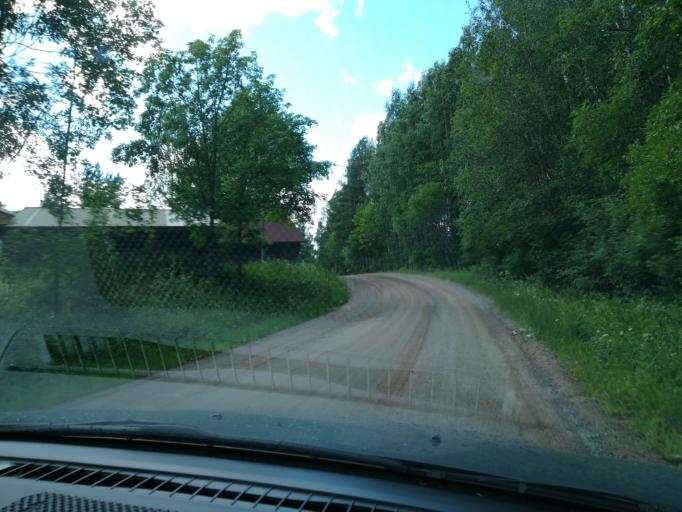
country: FI
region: South Karelia
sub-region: Lappeenranta
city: Savitaipale
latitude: 61.2976
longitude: 27.6474
